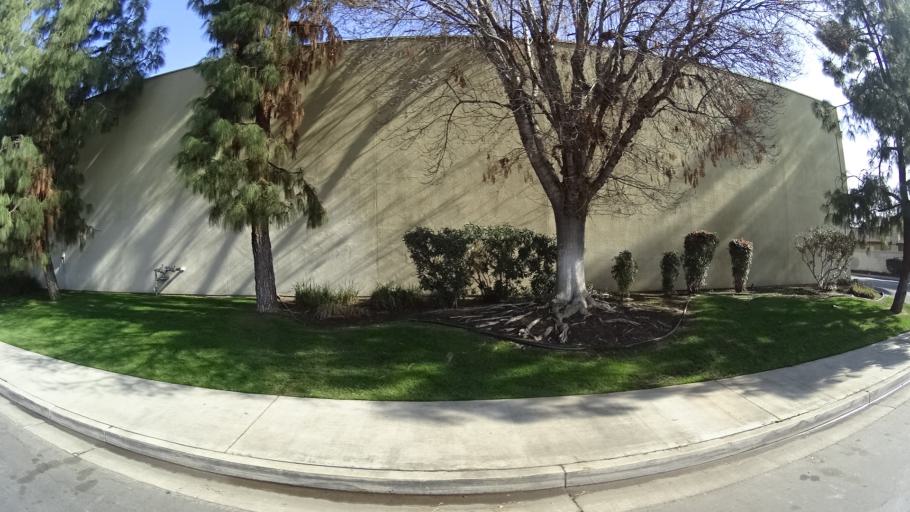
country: US
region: California
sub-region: Kern County
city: Bakersfield
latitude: 35.3383
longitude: -119.0562
